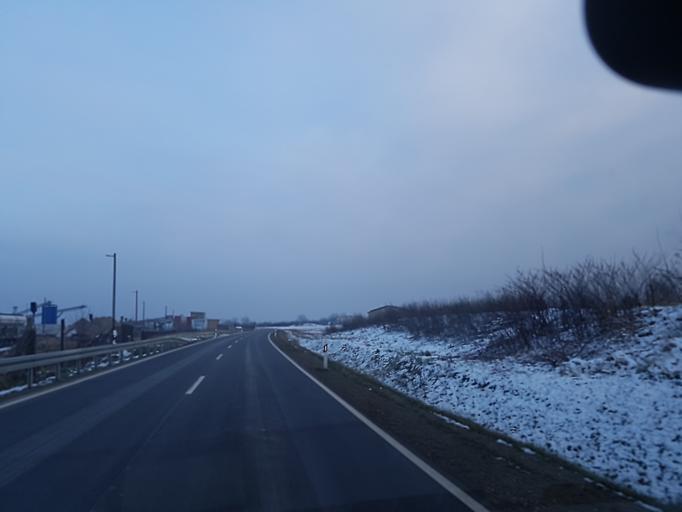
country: DE
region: Brandenburg
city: Muhlberg
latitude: 51.4364
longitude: 13.2320
